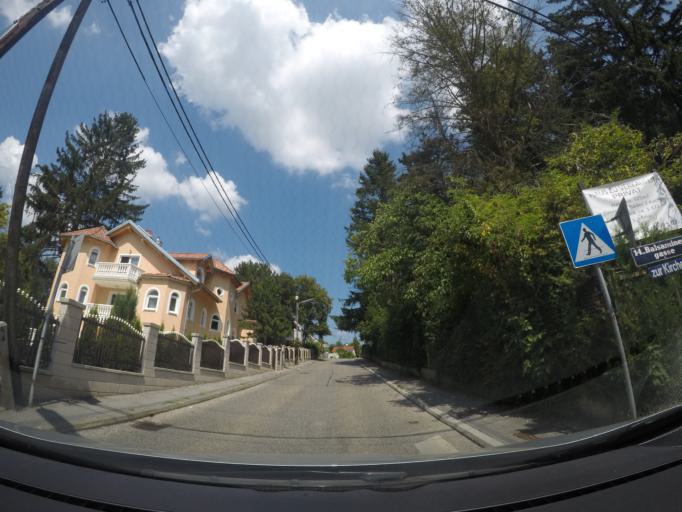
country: AT
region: Lower Austria
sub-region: Politischer Bezirk Wien-Umgebung
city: Purkersdorf
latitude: 48.2185
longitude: 16.2500
